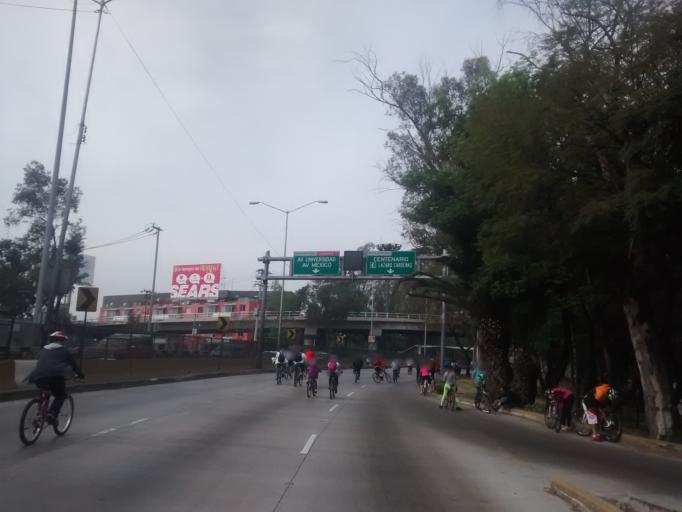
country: MX
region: Mexico City
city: Colonia Nativitas
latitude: 19.3567
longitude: -99.1334
